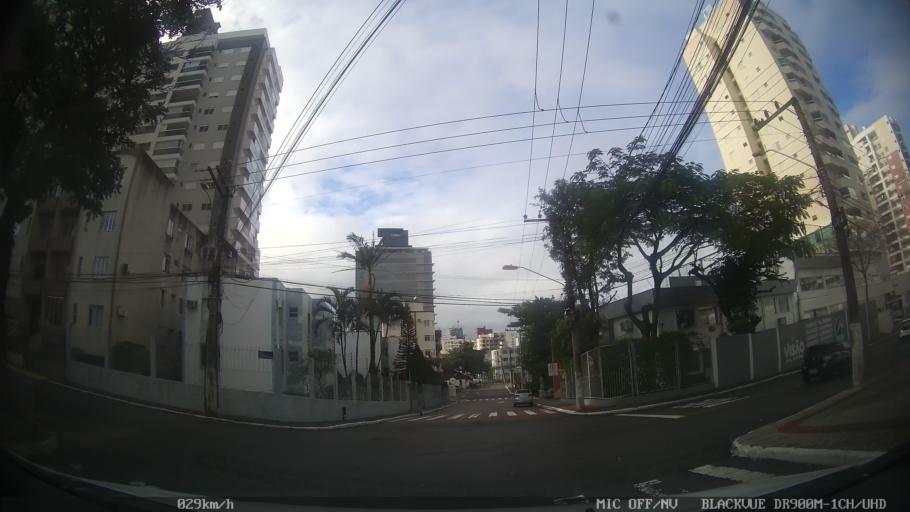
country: BR
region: Santa Catarina
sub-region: Sao Jose
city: Campinas
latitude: -27.5914
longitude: -48.6150
